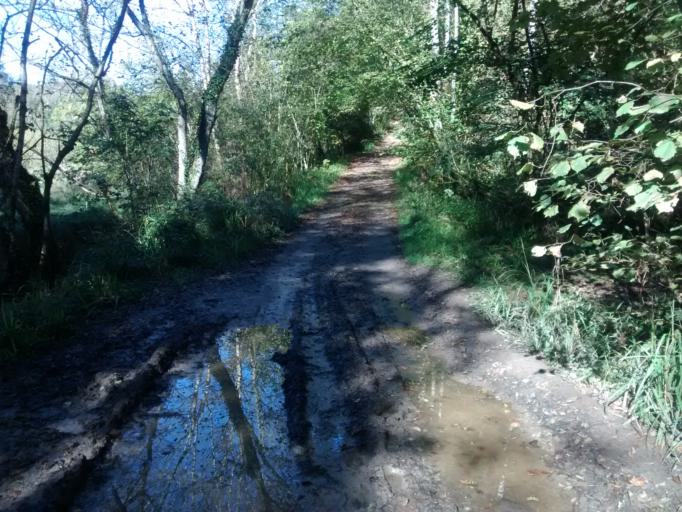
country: ES
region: Asturias
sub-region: Province of Asturias
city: Colunga
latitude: 43.4629
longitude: -5.2369
